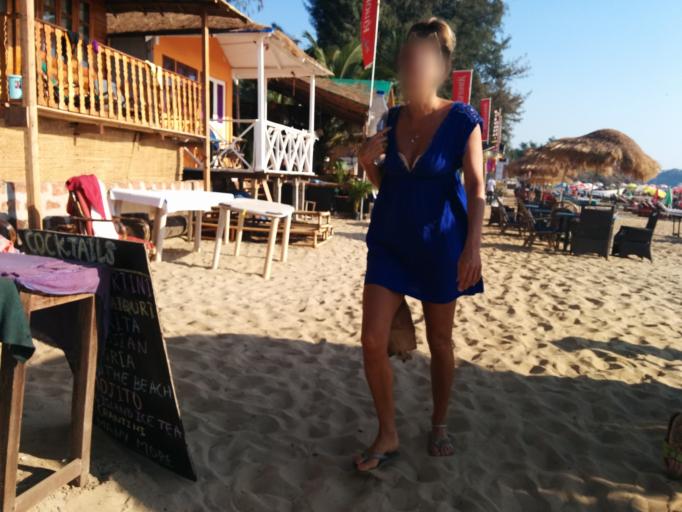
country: IN
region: Karnataka
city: Canacona
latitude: 14.9972
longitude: 74.0340
